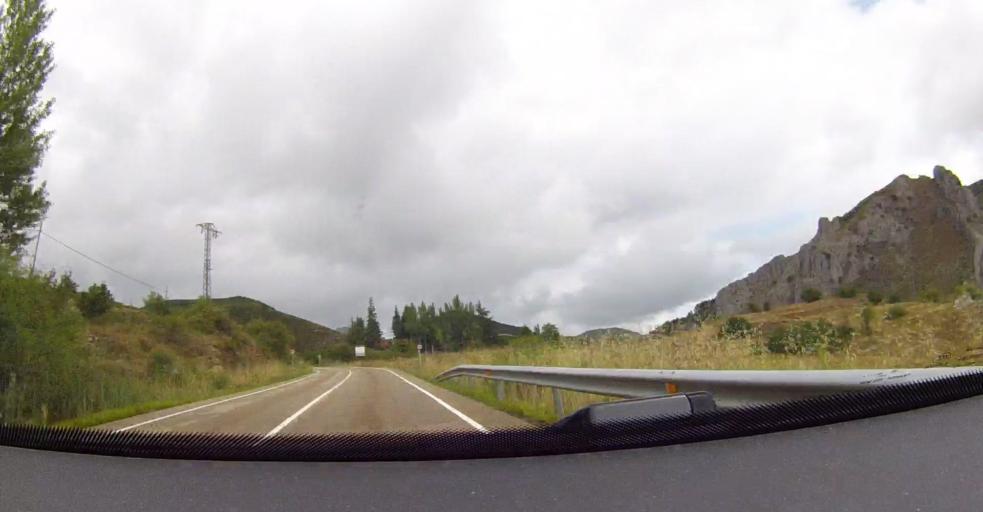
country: ES
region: Castille and Leon
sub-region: Provincia de Leon
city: Bonar
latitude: 42.9034
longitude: -5.3123
